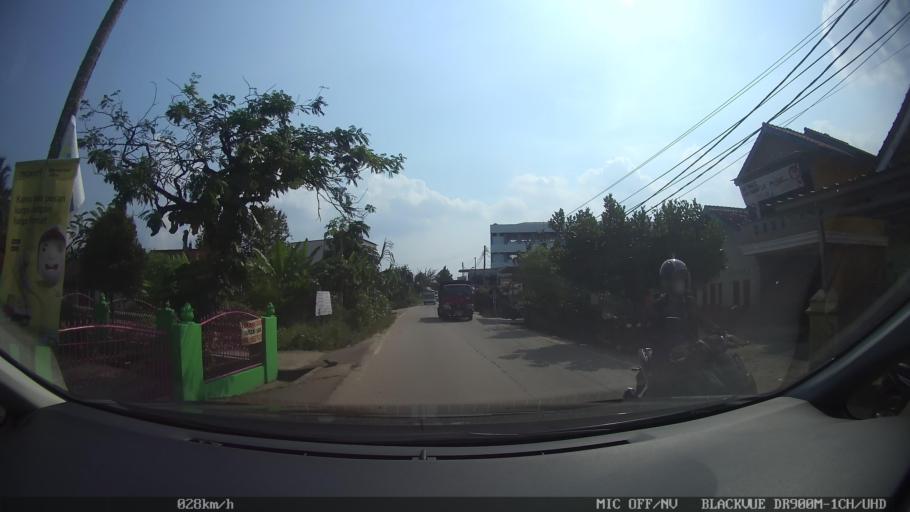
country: ID
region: Lampung
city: Natar
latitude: -5.3117
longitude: 105.1987
